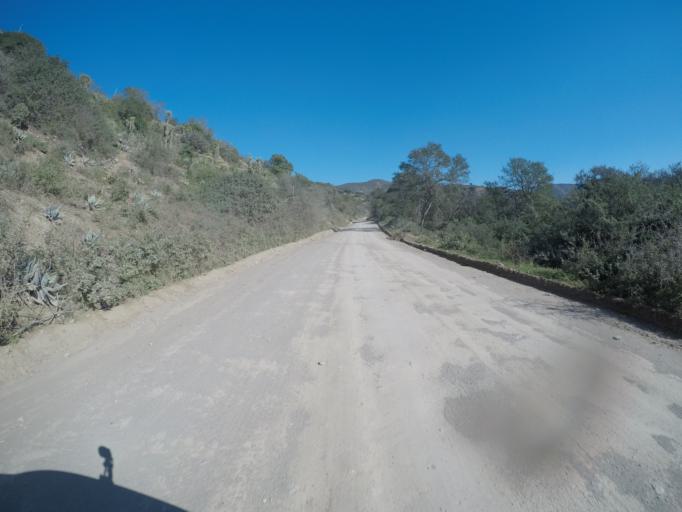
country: ZA
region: Eastern Cape
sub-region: Cacadu District Municipality
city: Kruisfontein
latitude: -33.6710
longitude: 24.5733
